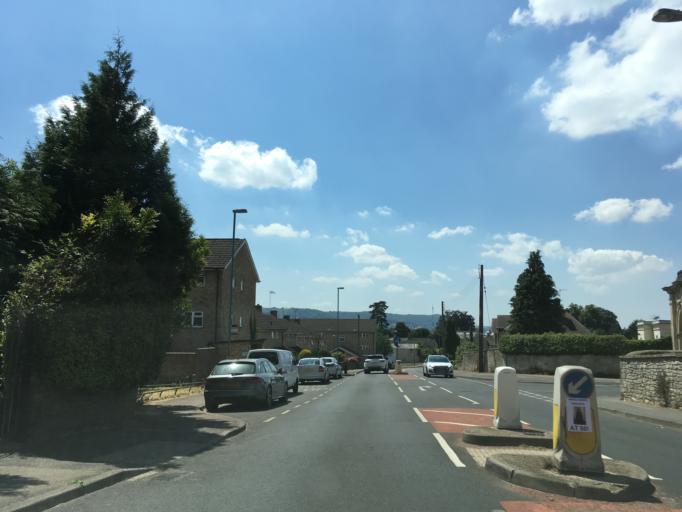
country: GB
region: England
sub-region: Gloucestershire
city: Stroud
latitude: 51.7506
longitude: -2.2356
